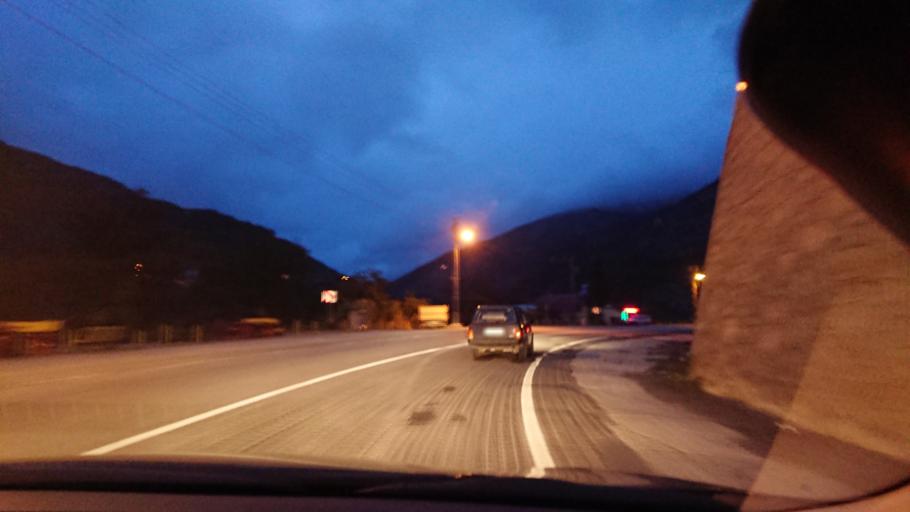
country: TR
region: Gumushane
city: Kurtun
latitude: 40.6723
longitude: 39.1384
